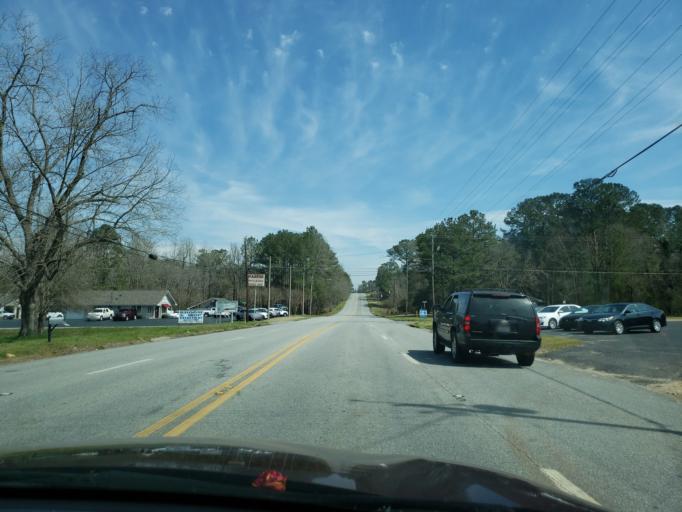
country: US
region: Alabama
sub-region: Elmore County
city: Tallassee
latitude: 32.5517
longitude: -85.8504
